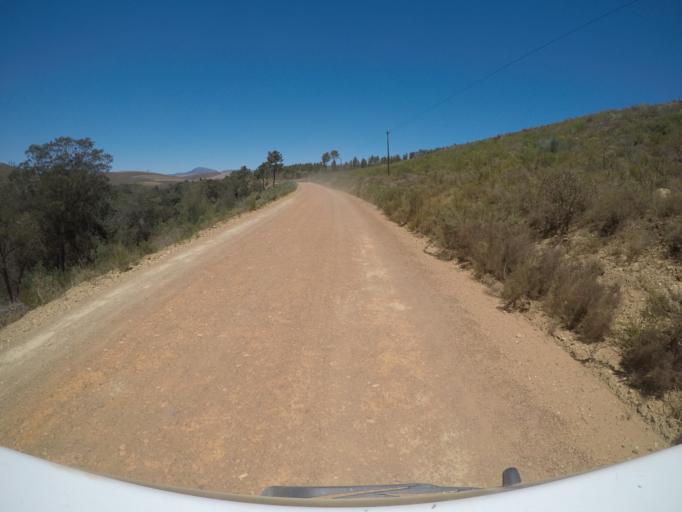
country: ZA
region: Western Cape
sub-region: Overberg District Municipality
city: Caledon
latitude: -34.1828
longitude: 19.2227
